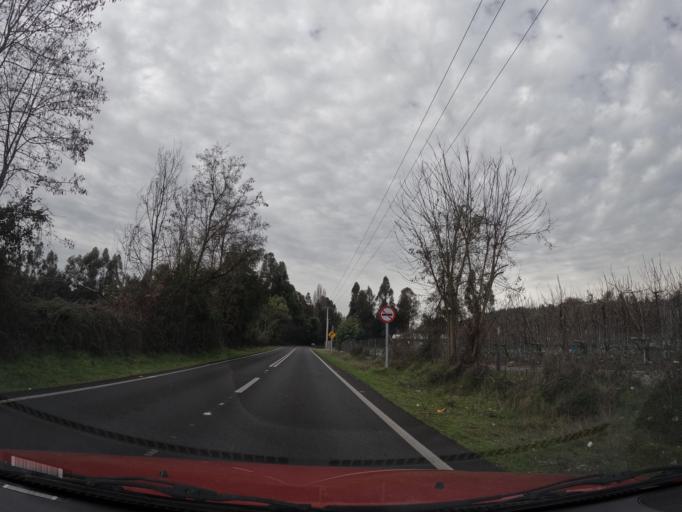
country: CL
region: Maule
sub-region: Provincia de Linares
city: Linares
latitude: -35.9119
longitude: -71.4896
